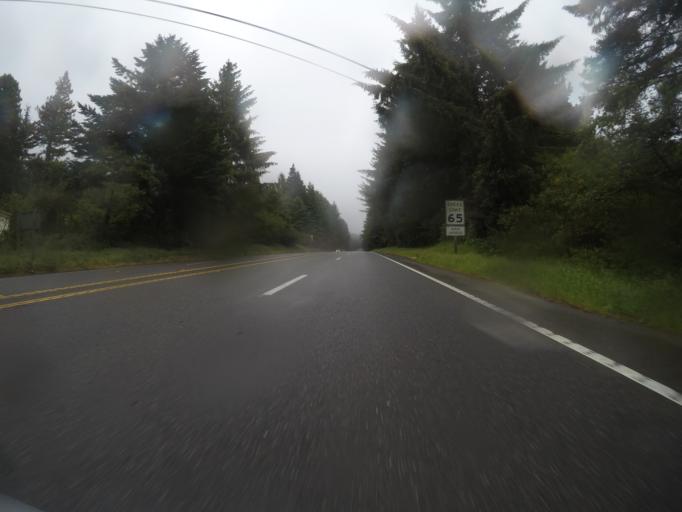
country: US
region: California
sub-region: Humboldt County
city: Westhaven-Moonstone
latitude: 41.0598
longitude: -124.1349
